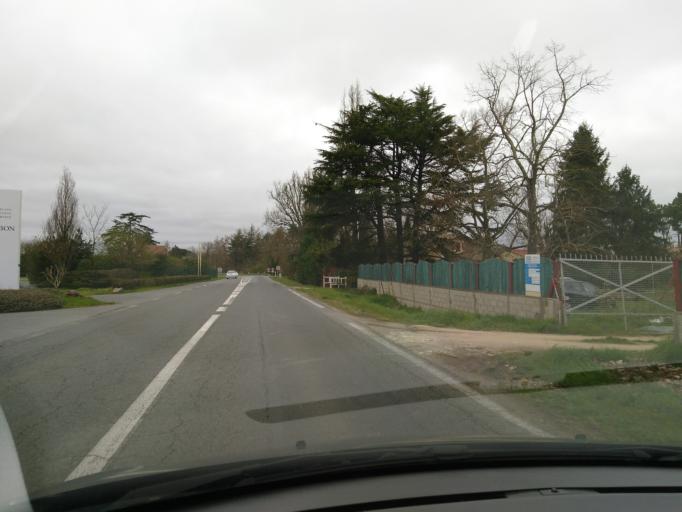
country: FR
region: Aquitaine
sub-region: Departement de la Dordogne
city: Bergerac
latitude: 44.8352
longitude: 0.4944
